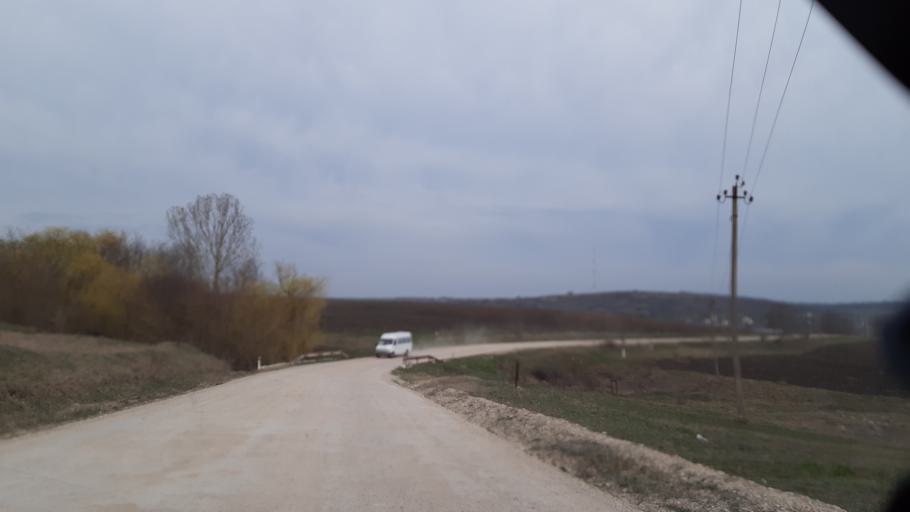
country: MD
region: Soldanesti
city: Soldanesti
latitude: 47.6797
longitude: 28.7870
